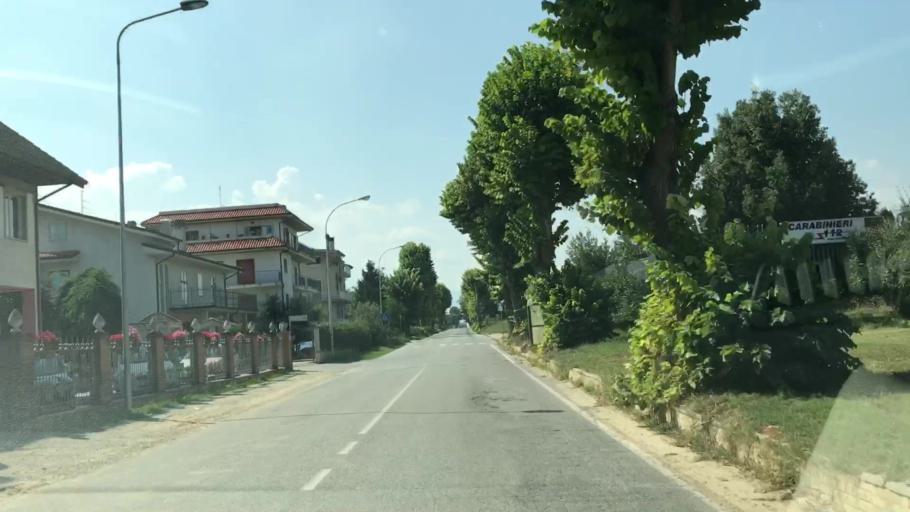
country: IT
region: The Marches
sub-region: Provincia di Ascoli Piceno
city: Stella
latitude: 42.8831
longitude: 13.7967
